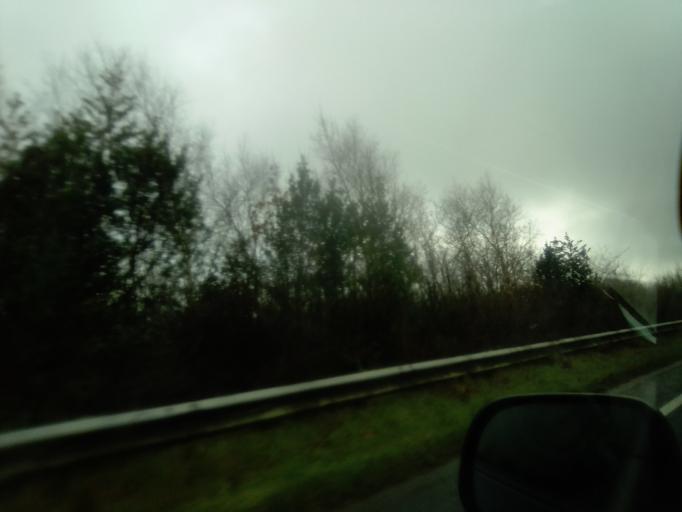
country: GB
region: Northern Ireland
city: Newtownstewart
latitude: 54.7192
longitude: -7.3665
